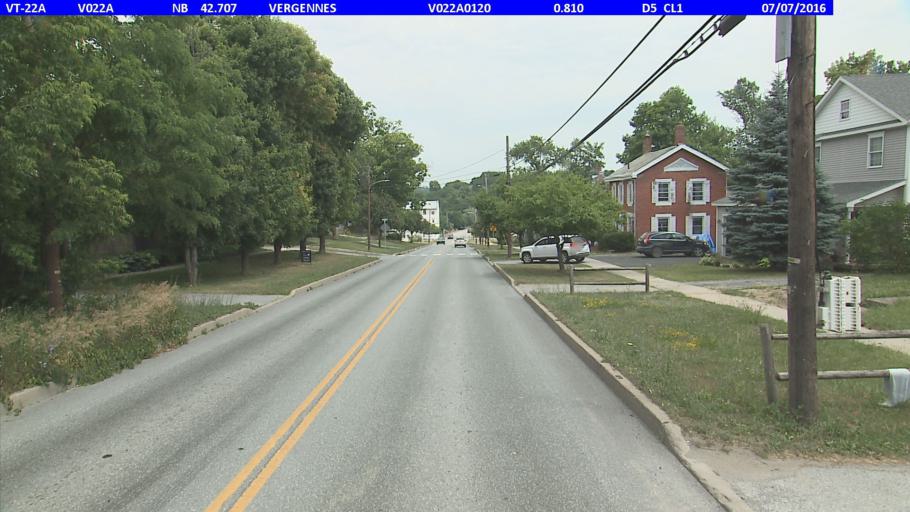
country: US
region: Vermont
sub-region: Addison County
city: Vergennes
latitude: 44.1640
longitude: -73.2581
